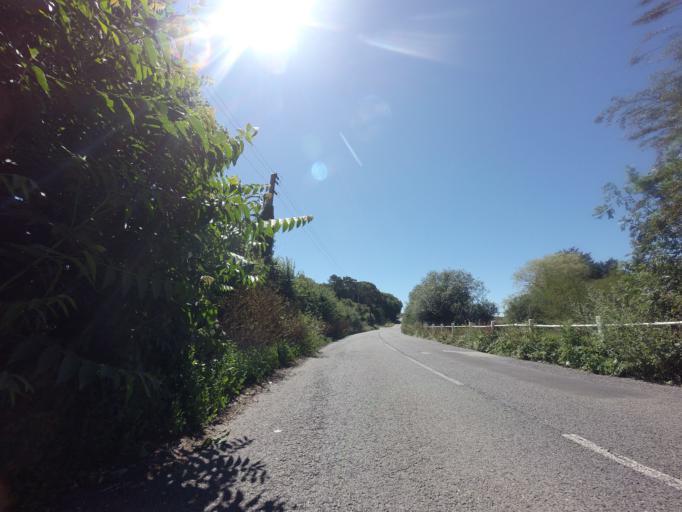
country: GB
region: England
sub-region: Kent
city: Eastry
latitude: 51.2401
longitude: 1.3076
